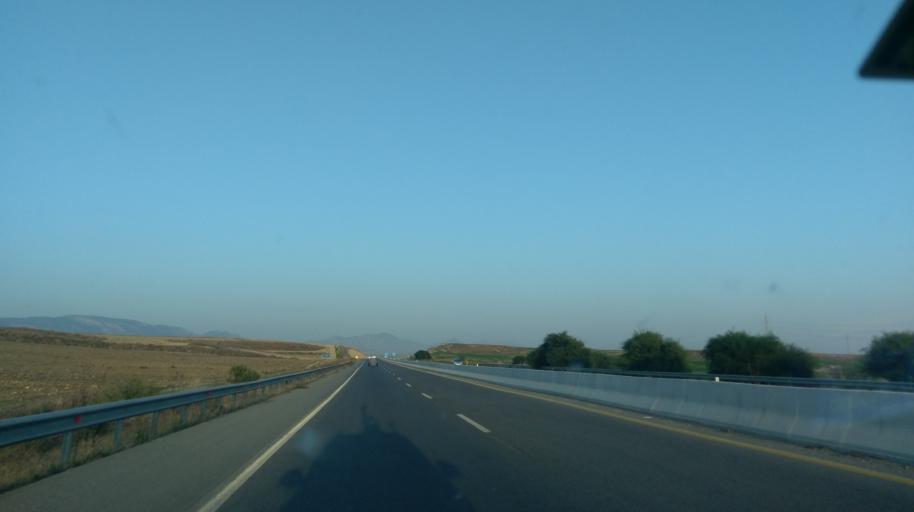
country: CY
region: Lefkosia
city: Mammari
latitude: 35.2197
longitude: 33.1453
